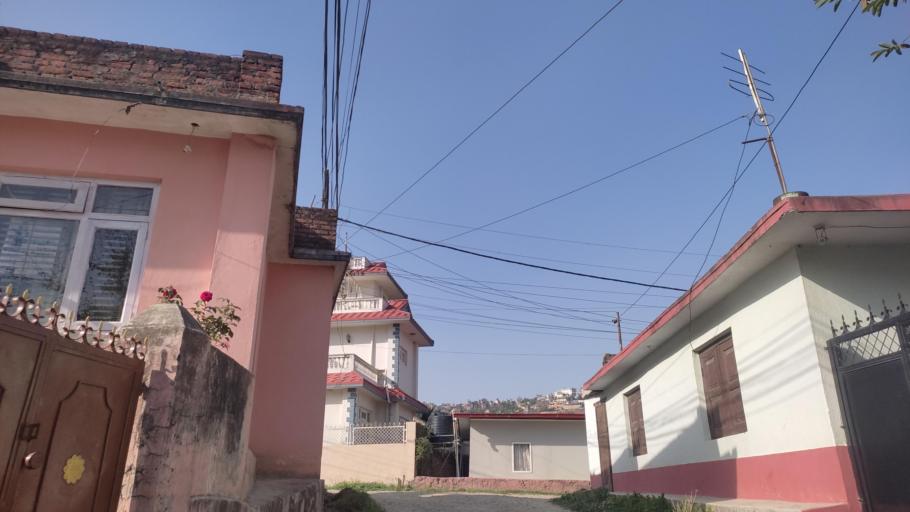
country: NP
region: Central Region
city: Kirtipur
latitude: 27.6560
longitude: 85.2859
